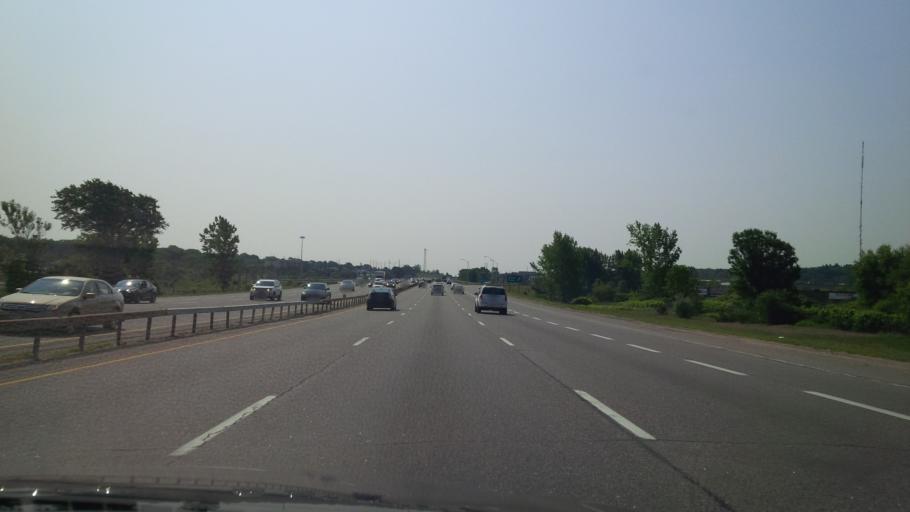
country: CA
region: Ontario
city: Barrie
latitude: 44.3662
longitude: -79.7023
